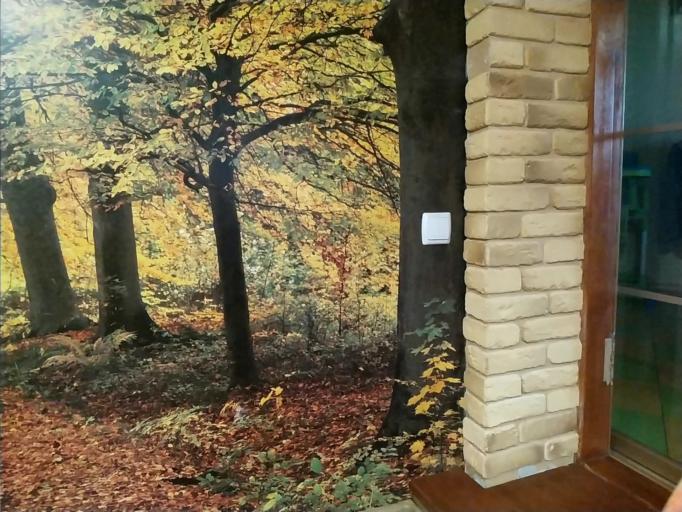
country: RU
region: Smolensk
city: Safonovo
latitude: 55.1942
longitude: 33.1335
